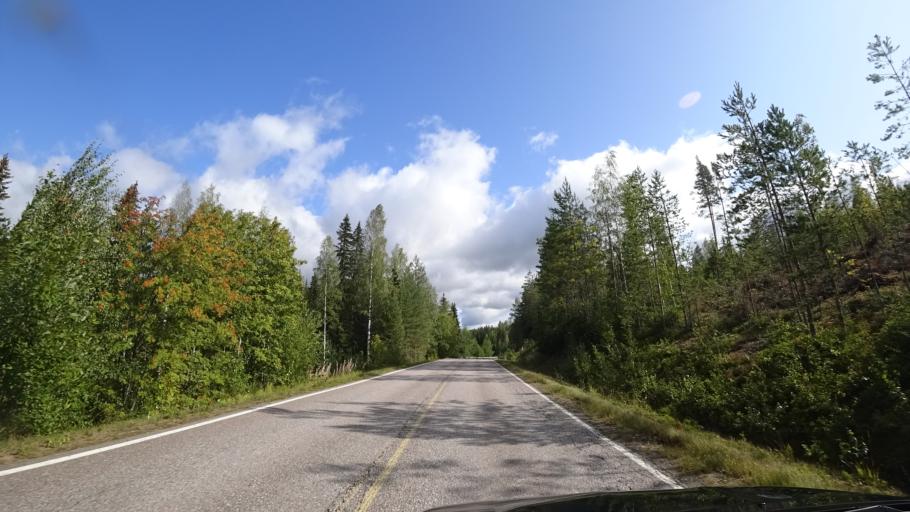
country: FI
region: Haeme
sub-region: Riihimaeki
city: Oitti
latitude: 60.6789
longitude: 24.9931
